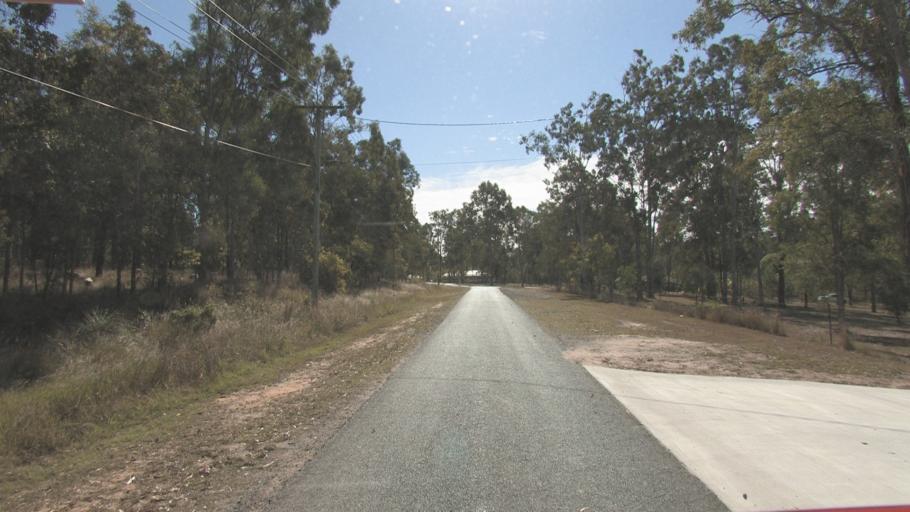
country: AU
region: Queensland
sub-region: Ipswich
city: Springfield Lakes
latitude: -27.7056
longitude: 152.9415
